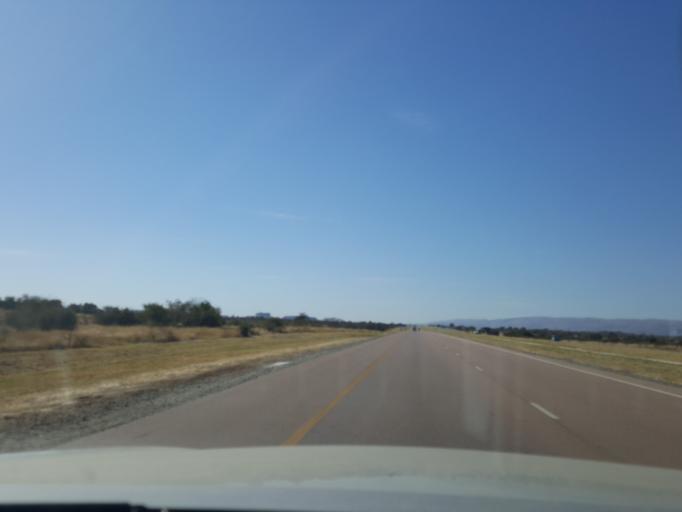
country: ZA
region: North-West
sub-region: Bojanala Platinum District Municipality
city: Brits
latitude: -25.7372
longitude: 27.5666
